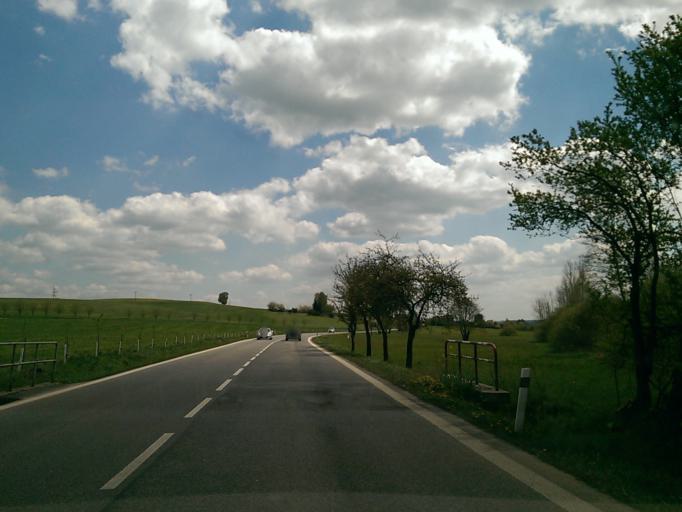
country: CZ
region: Liberecky
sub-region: Okres Semily
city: Turnov
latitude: 50.5585
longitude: 15.2046
